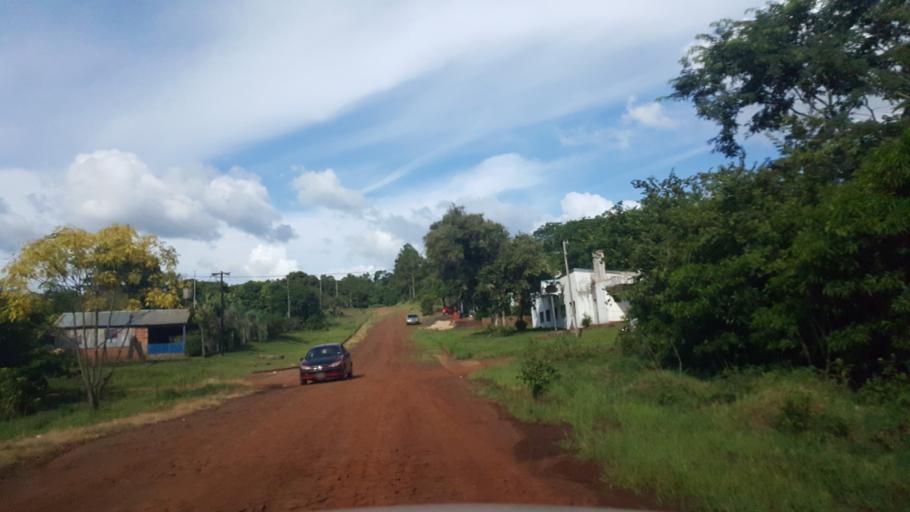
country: AR
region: Misiones
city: Santa Ana
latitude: -27.3667
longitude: -55.5751
